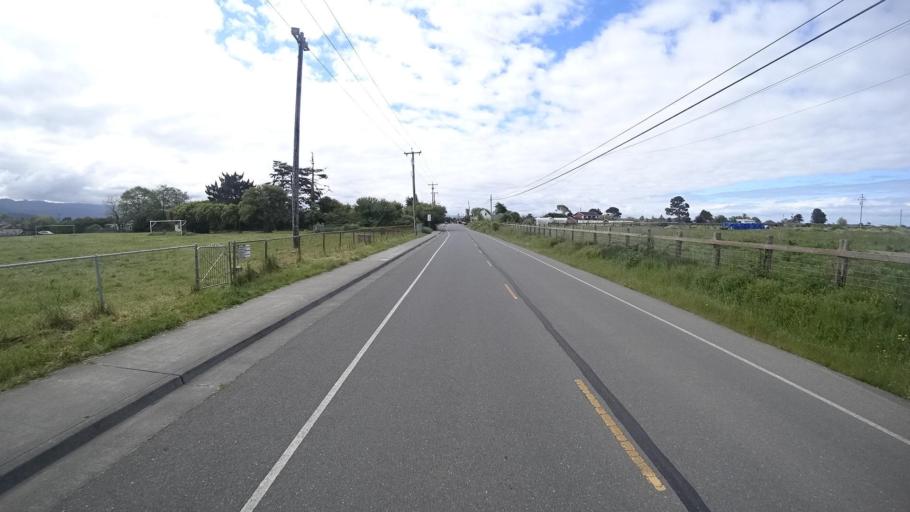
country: US
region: California
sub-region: Humboldt County
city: Arcata
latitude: 40.8773
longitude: -124.1012
